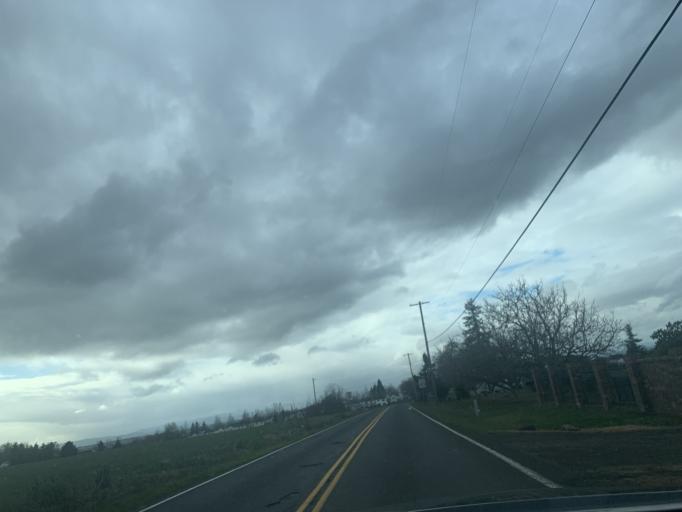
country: US
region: Oregon
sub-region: Washington County
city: Oak Hills
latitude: 45.5675
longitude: -122.8206
